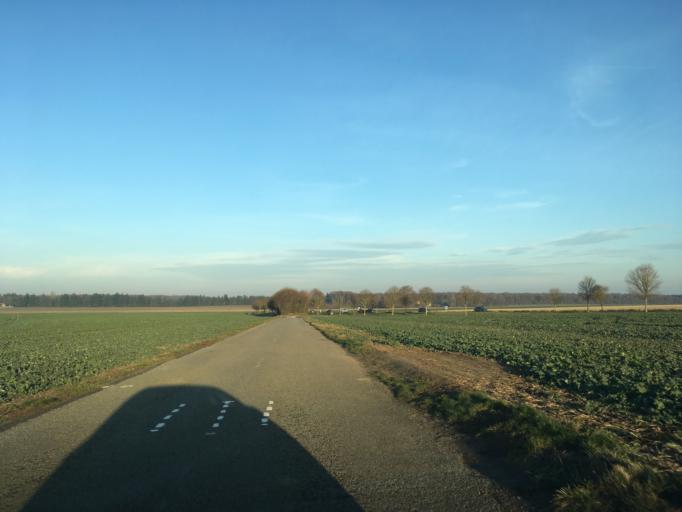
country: FR
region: Haute-Normandie
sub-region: Departement de l'Eure
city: Saint-Marcel
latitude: 49.0689
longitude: 1.4237
